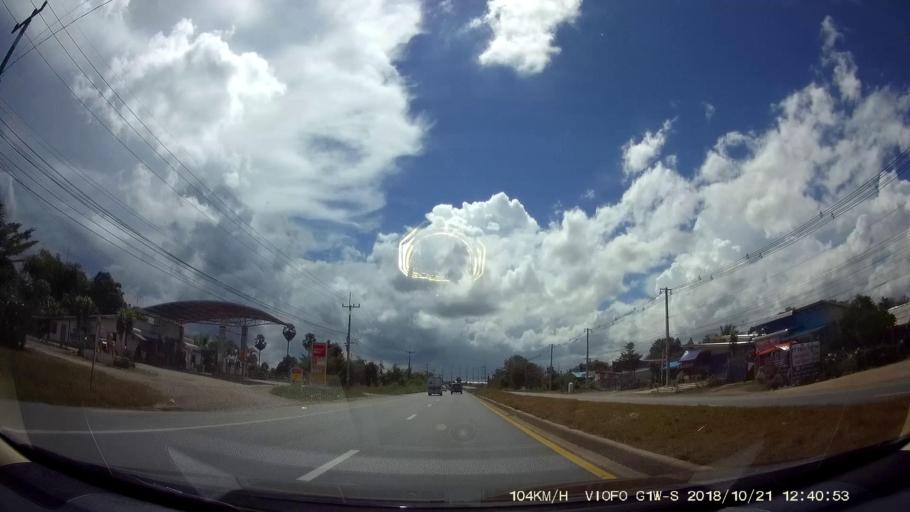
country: TH
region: Nakhon Ratchasima
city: Amphoe Sikhiu
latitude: 15.0192
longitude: 101.6901
